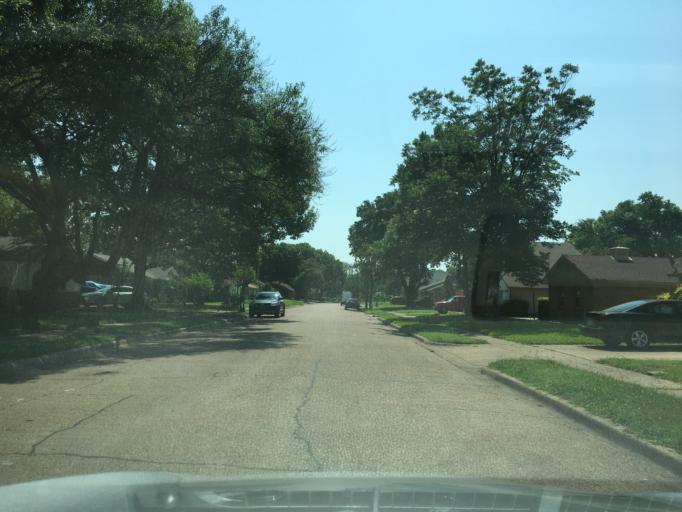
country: US
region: Texas
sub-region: Dallas County
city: Richardson
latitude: 32.9235
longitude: -96.6983
